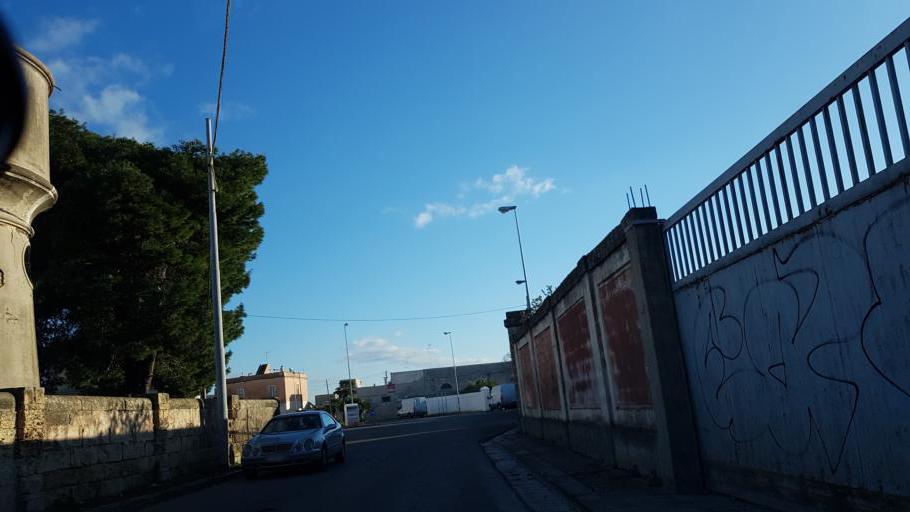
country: IT
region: Apulia
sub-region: Provincia di Lecce
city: Squinzano
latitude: 40.4397
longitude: 18.0452
